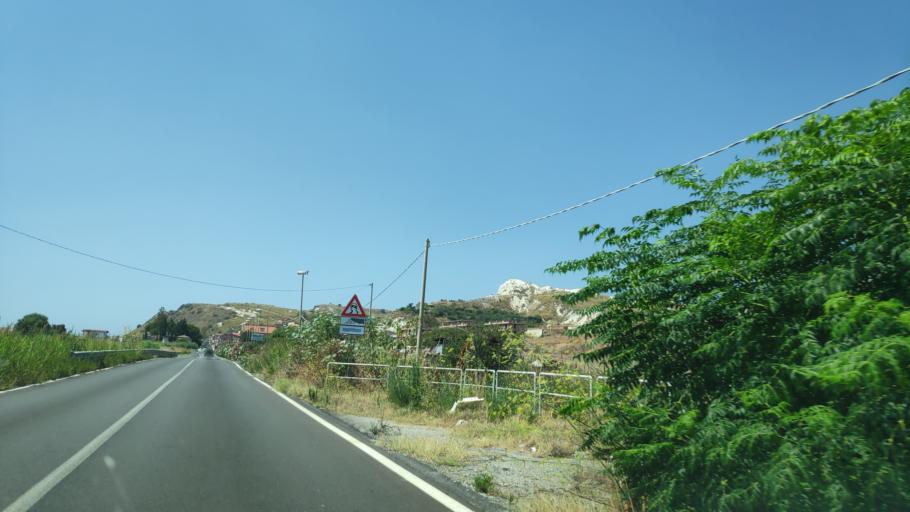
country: IT
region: Calabria
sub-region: Provincia di Reggio Calabria
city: Weather Station
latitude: 37.9346
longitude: 16.0717
